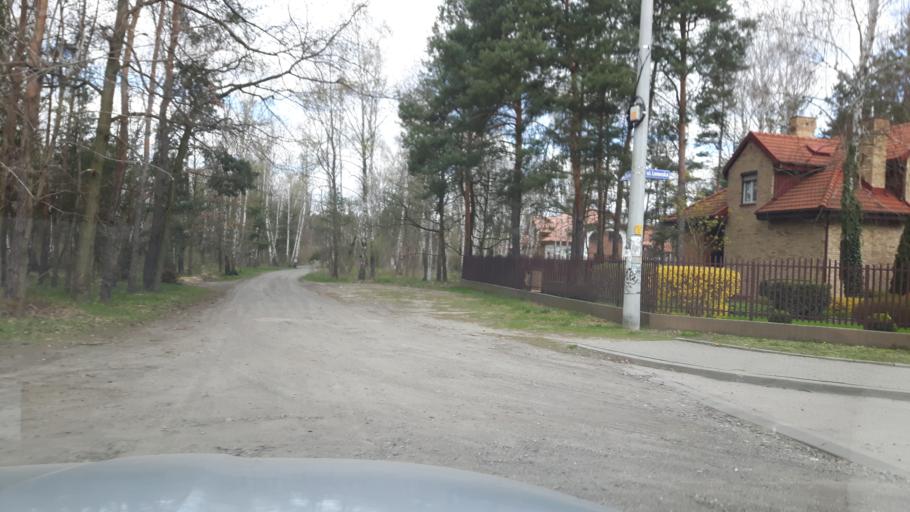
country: PL
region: Masovian Voivodeship
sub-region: Powiat wolominski
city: Wolomin
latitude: 52.3486
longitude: 21.2213
